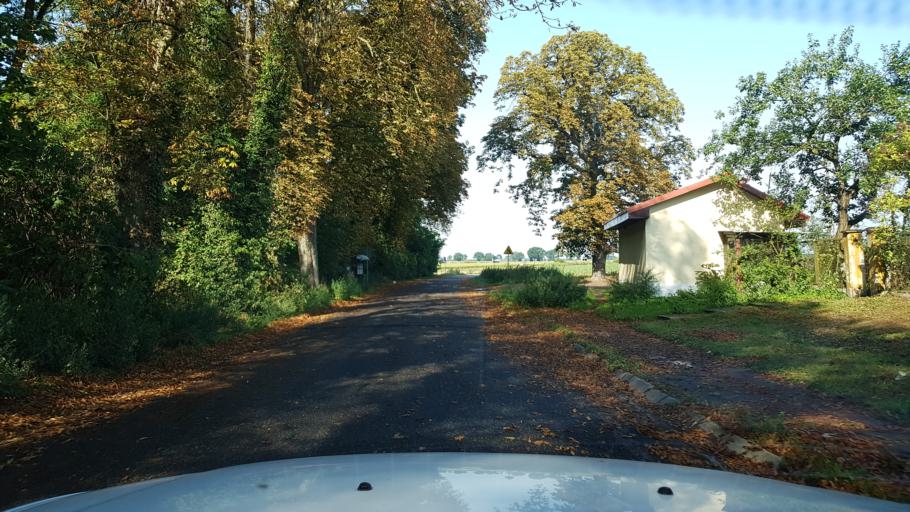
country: PL
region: West Pomeranian Voivodeship
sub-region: Powiat stargardzki
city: Dolice
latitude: 53.2370
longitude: 15.2231
